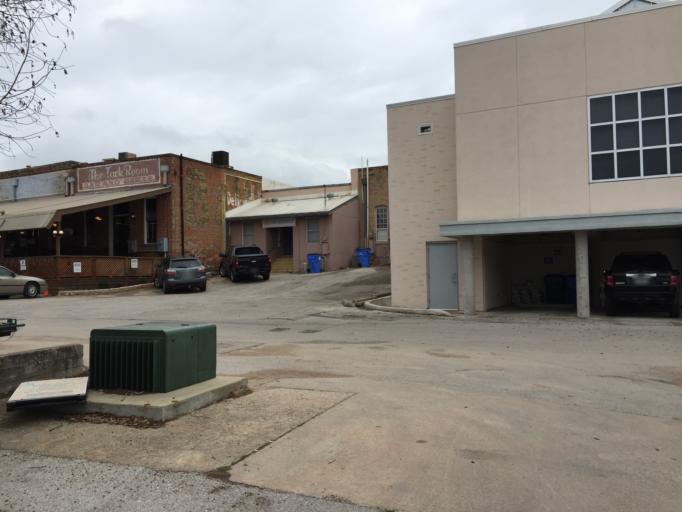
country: US
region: Texas
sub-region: Bastrop County
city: Bastrop
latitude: 30.1094
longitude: -97.3206
